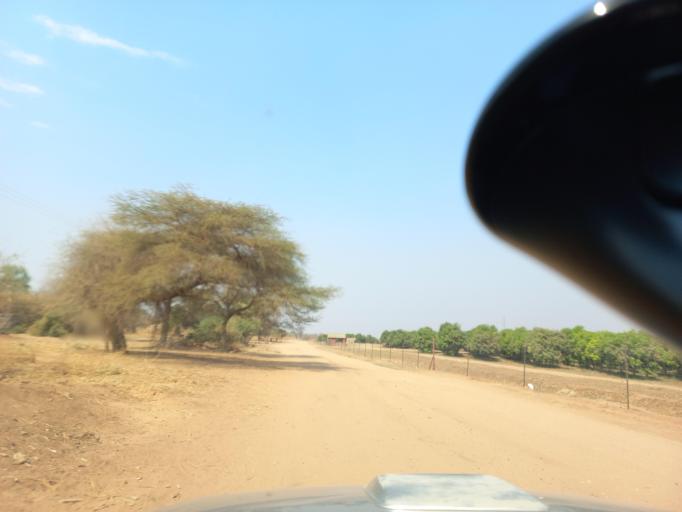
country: ZW
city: Chirundu
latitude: -15.9325
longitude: 28.9488
